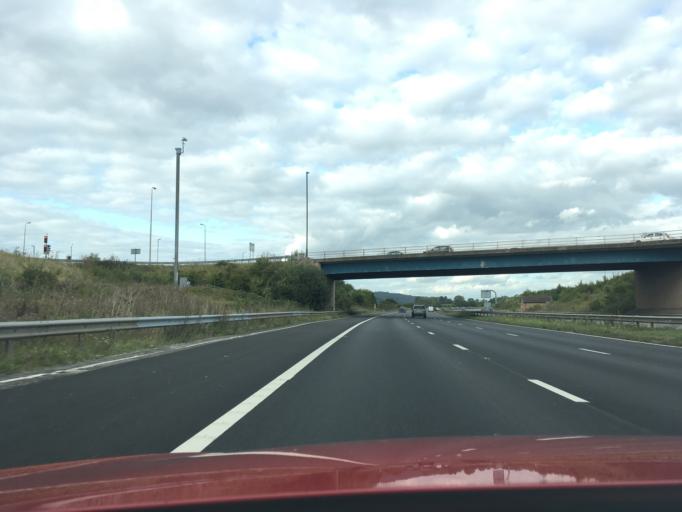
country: GB
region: England
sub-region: Gloucestershire
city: Stonehouse
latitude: 51.7976
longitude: -2.2899
